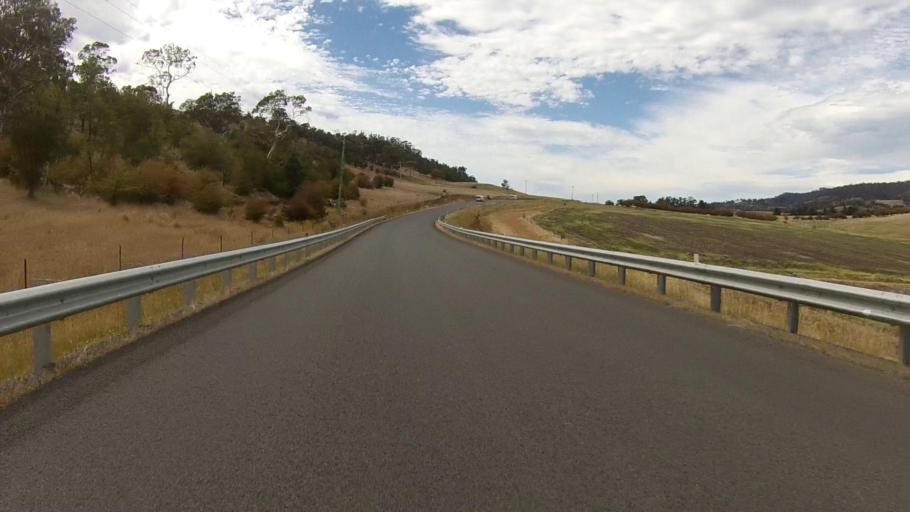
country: AU
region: Tasmania
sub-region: Brighton
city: Old Beach
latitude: -42.7218
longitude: 147.3383
